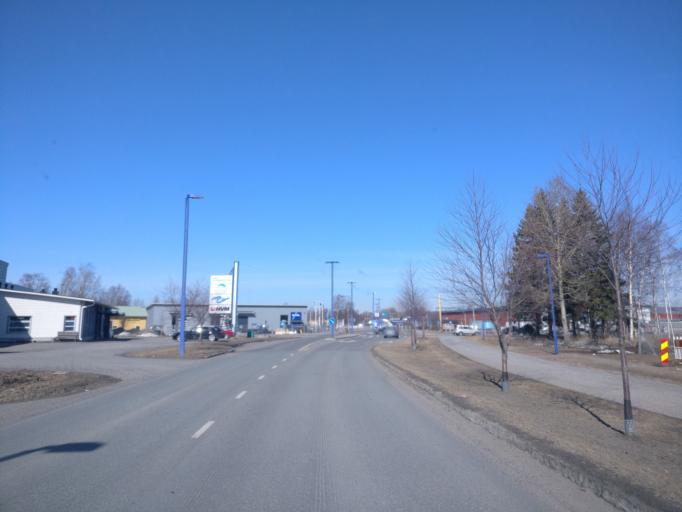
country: FI
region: Lapland
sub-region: Kemi-Tornio
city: Kemi
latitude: 65.7402
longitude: 24.5772
